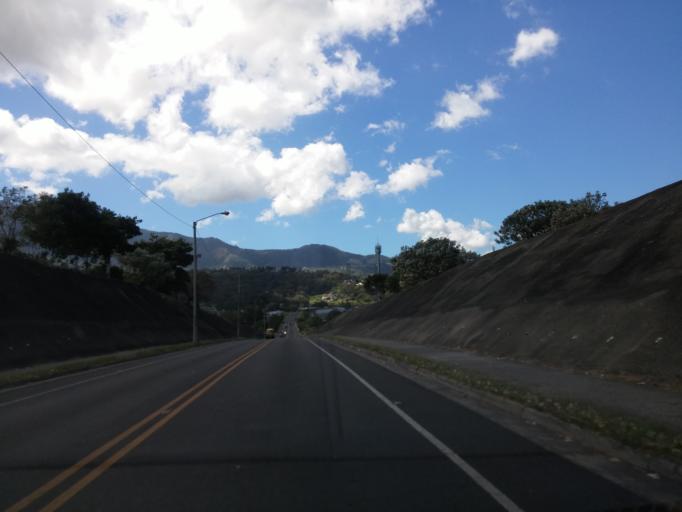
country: CR
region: San Jose
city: San Felipe
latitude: 9.9214
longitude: -84.1102
